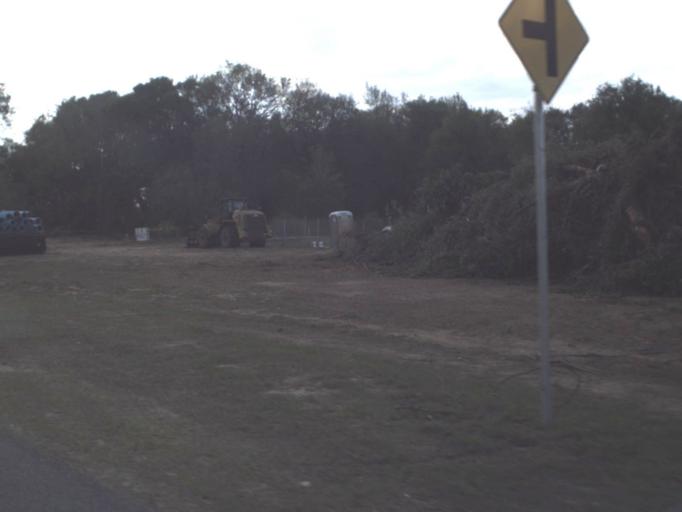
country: US
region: Florida
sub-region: Lake County
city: Mount Dora
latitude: 28.8006
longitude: -81.6045
